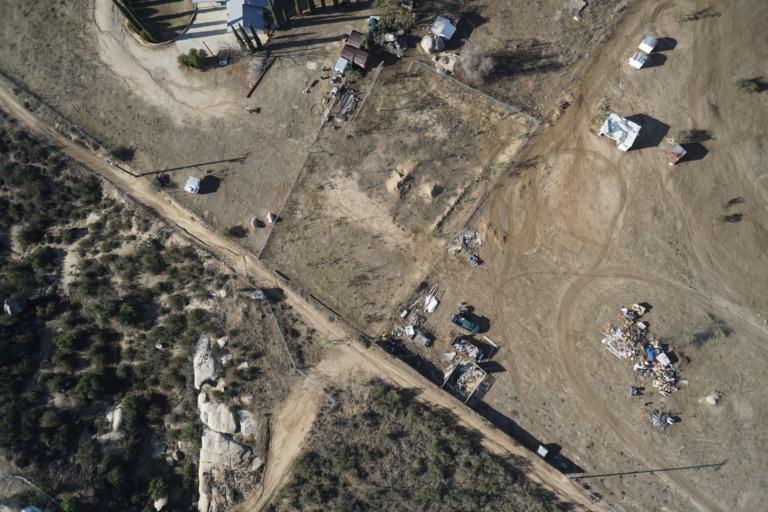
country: US
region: California
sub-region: Riverside County
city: Valle Vista
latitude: 33.6304
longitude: -116.8944
